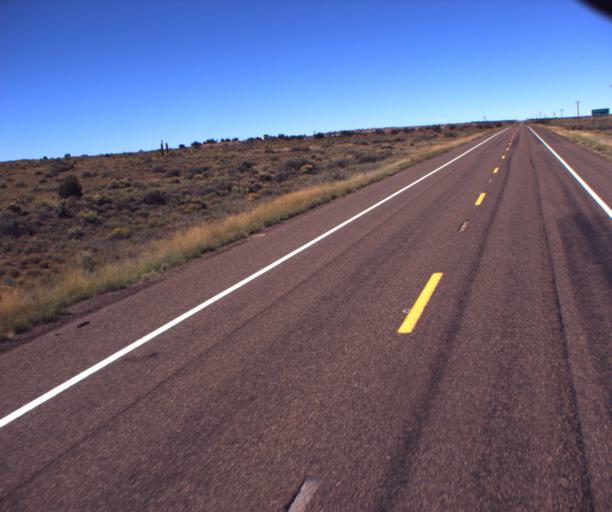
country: US
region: Arizona
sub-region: Apache County
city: Saint Johns
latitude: 34.6217
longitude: -109.6647
